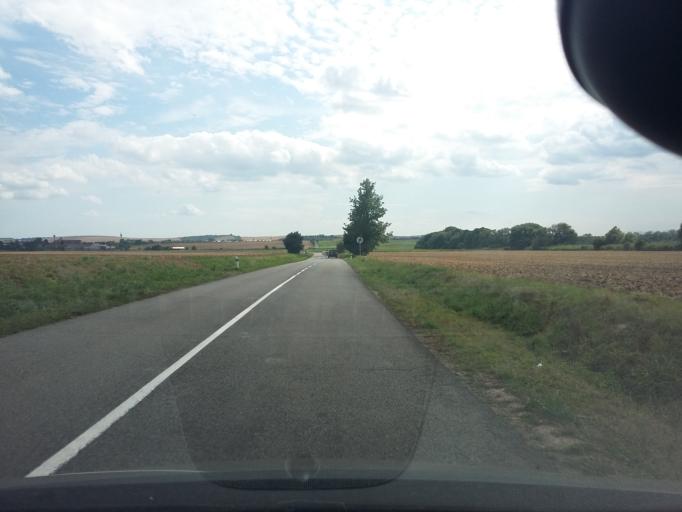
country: SK
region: Trnavsky
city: Gbely
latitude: 48.7431
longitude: 17.1706
